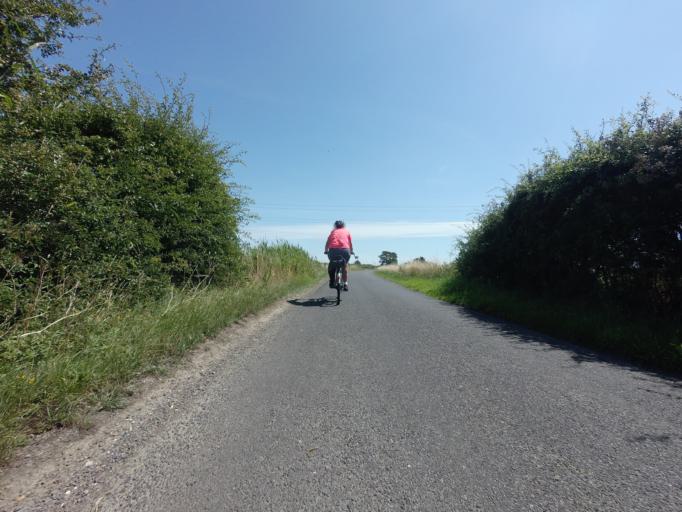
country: GB
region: England
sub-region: Kent
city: Lydd
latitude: 50.9777
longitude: 0.8983
